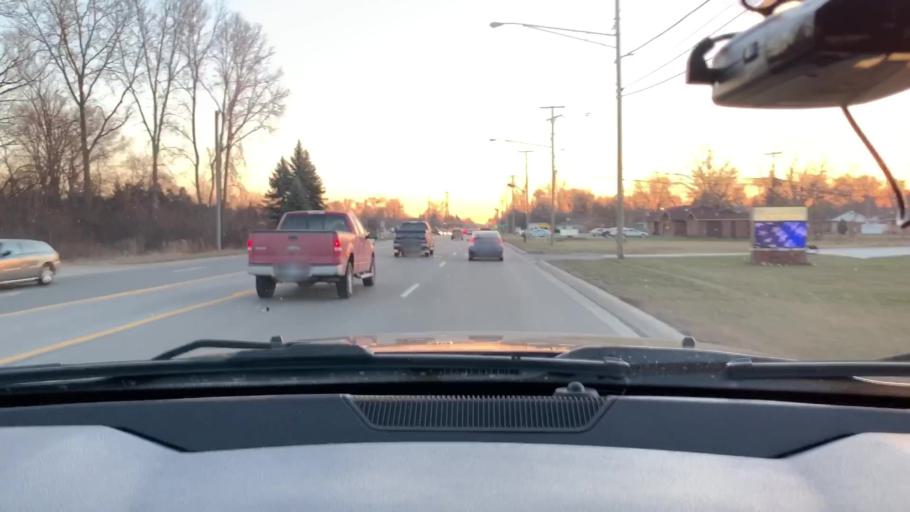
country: US
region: Michigan
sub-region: Wayne County
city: Woodhaven
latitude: 42.1267
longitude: -83.2740
